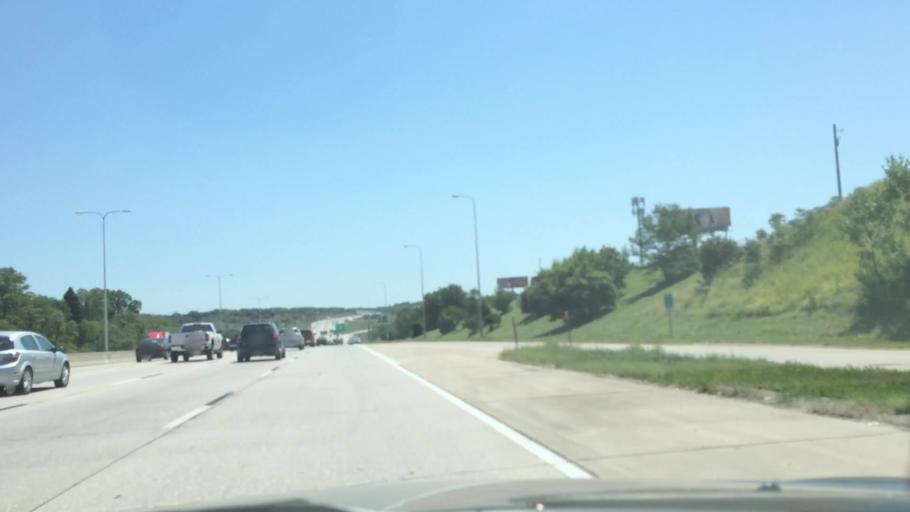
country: US
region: Nebraska
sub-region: Douglas County
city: Ralston
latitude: 41.2230
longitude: -96.0210
